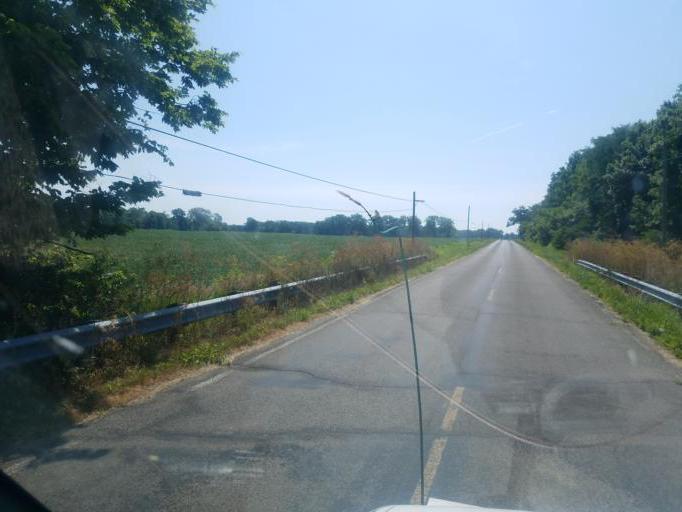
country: US
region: Ohio
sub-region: Champaign County
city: North Lewisburg
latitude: 40.2111
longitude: -83.4994
